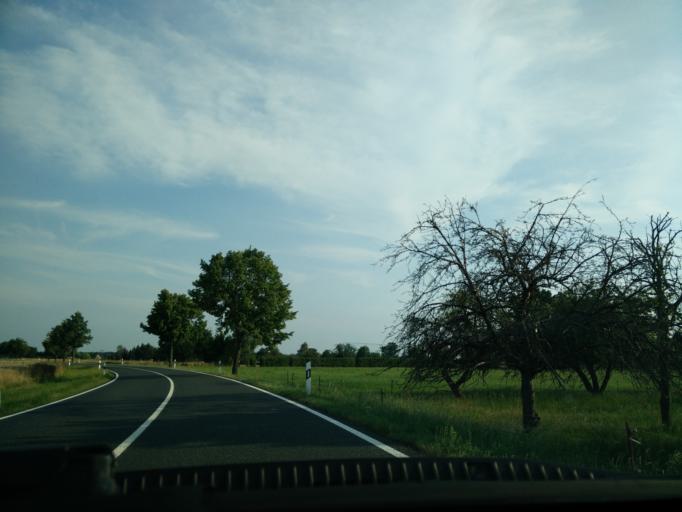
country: DE
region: Saxony
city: Frohburg
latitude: 51.0898
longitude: 12.5651
